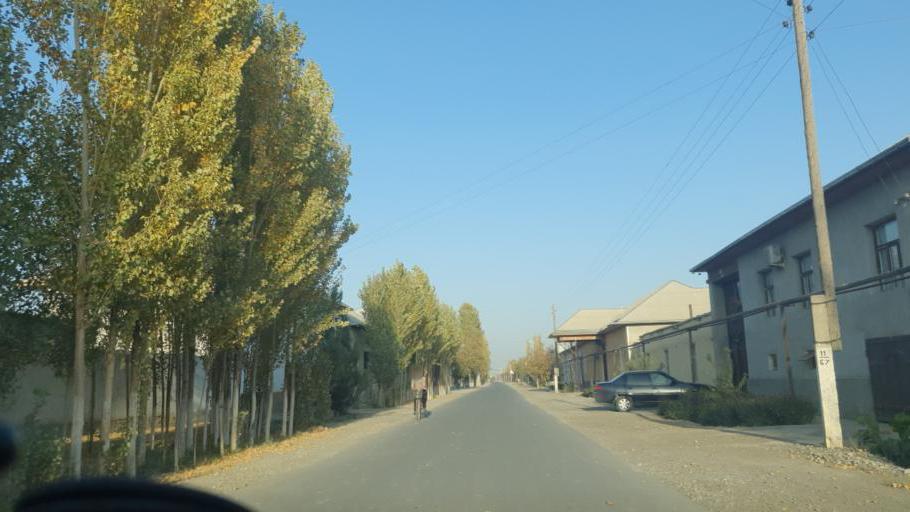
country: UZ
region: Fergana
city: Beshariq
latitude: 40.4646
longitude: 70.5521
